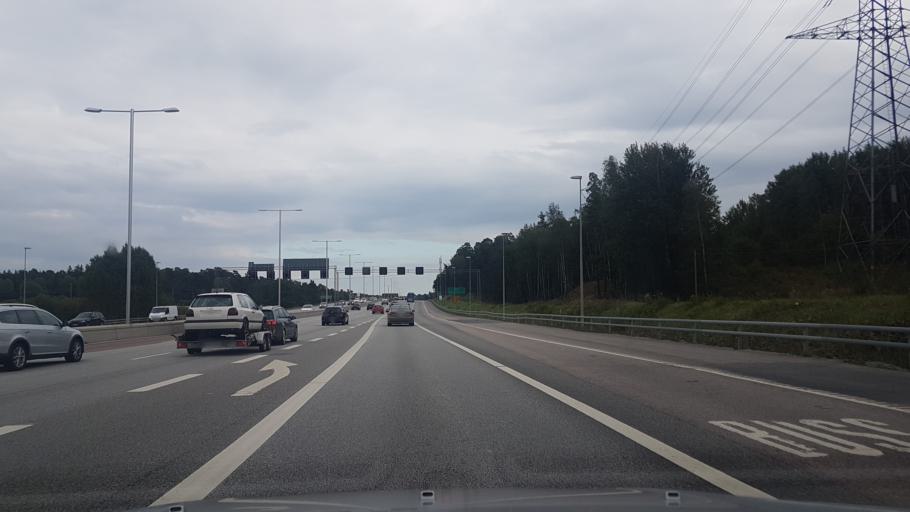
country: SE
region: Stockholm
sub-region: Solna Kommun
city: Rasunda
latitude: 59.3973
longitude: 17.9800
